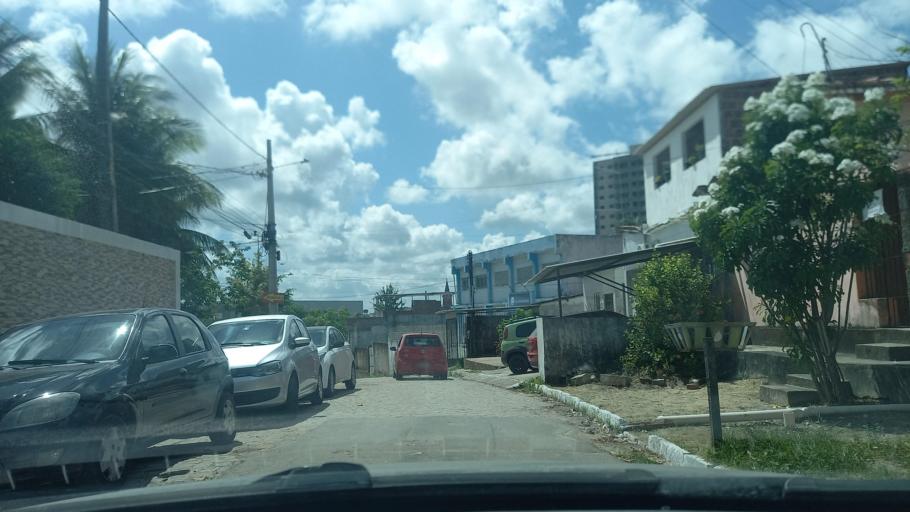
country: BR
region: Pernambuco
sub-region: Paulista
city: Paulista
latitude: -7.9404
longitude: -34.8749
